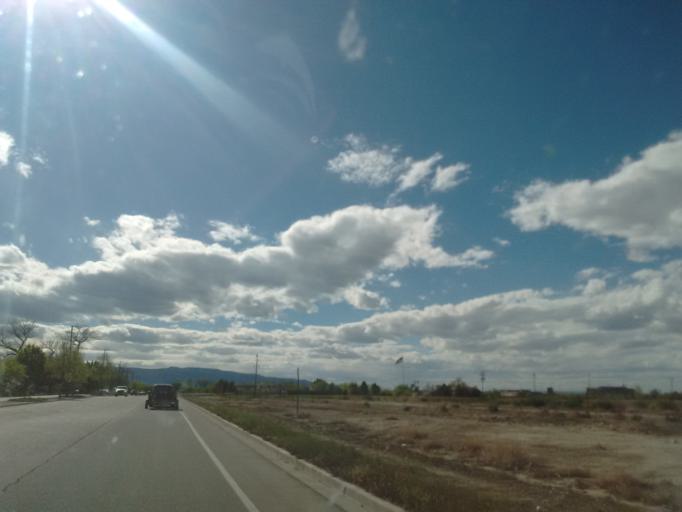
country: US
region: Colorado
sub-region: Mesa County
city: Grand Junction
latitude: 39.0629
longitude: -108.5227
